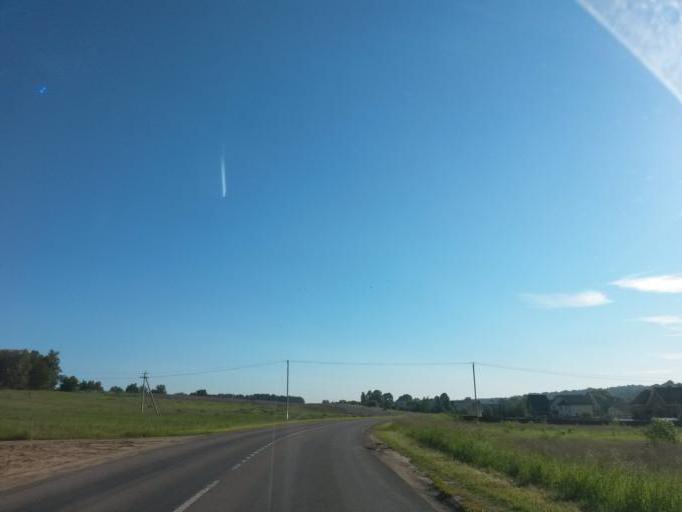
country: RU
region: Moskovskaya
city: Lyubuchany
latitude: 55.2852
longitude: 37.6220
